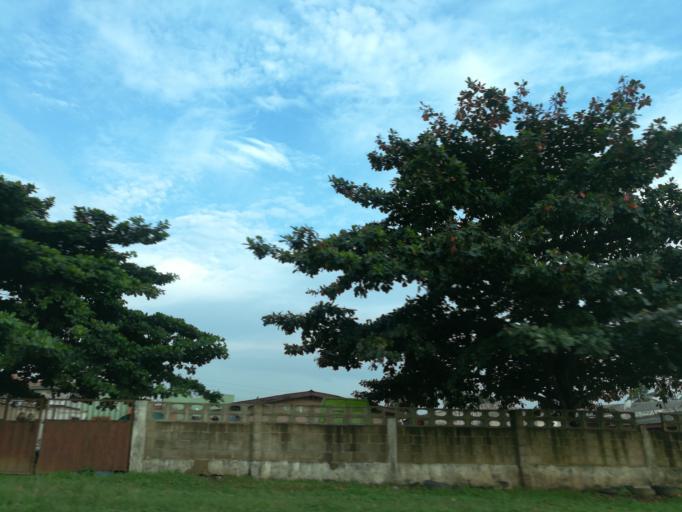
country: NG
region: Lagos
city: Oshodi
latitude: 6.5679
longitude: 3.3304
